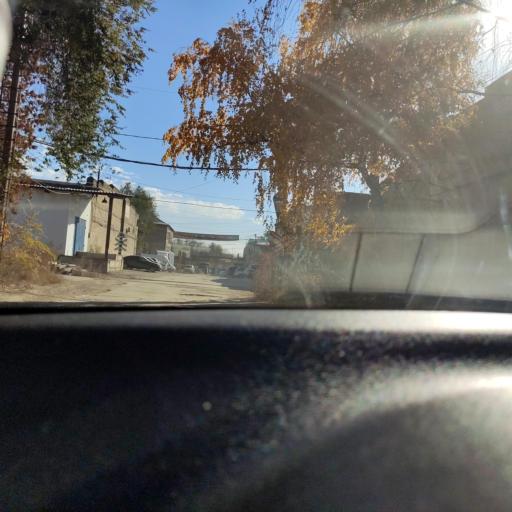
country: RU
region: Samara
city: Petra-Dubrava
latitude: 53.2465
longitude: 50.2993
